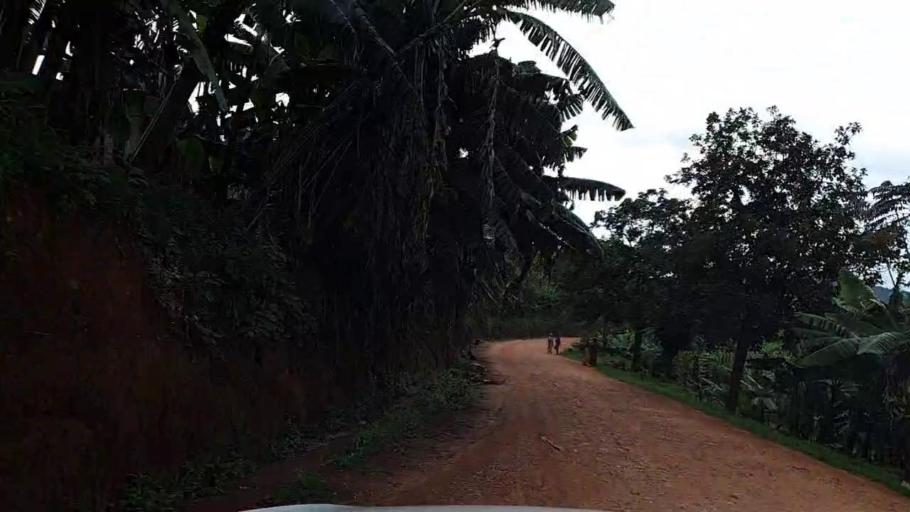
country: RW
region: Southern Province
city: Nyanza
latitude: -2.4160
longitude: 29.6683
